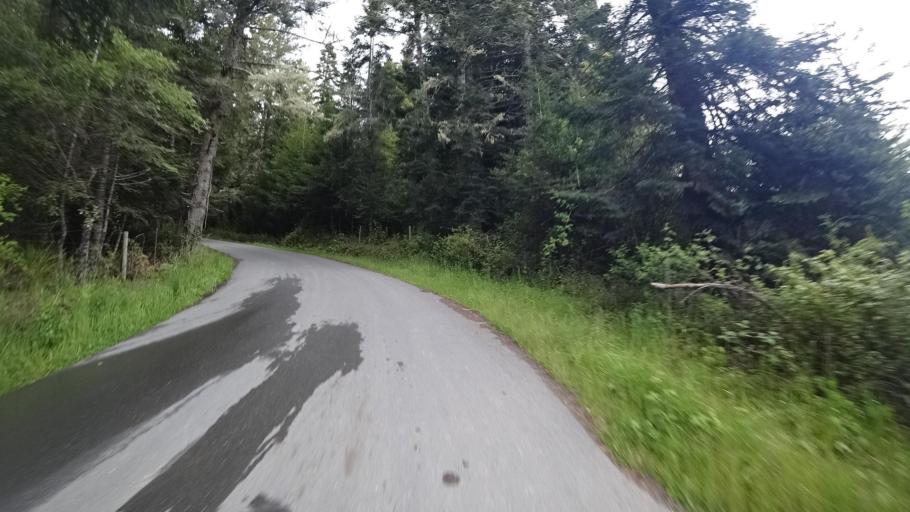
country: US
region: California
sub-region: Humboldt County
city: Blue Lake
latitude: 40.9044
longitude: -123.9848
